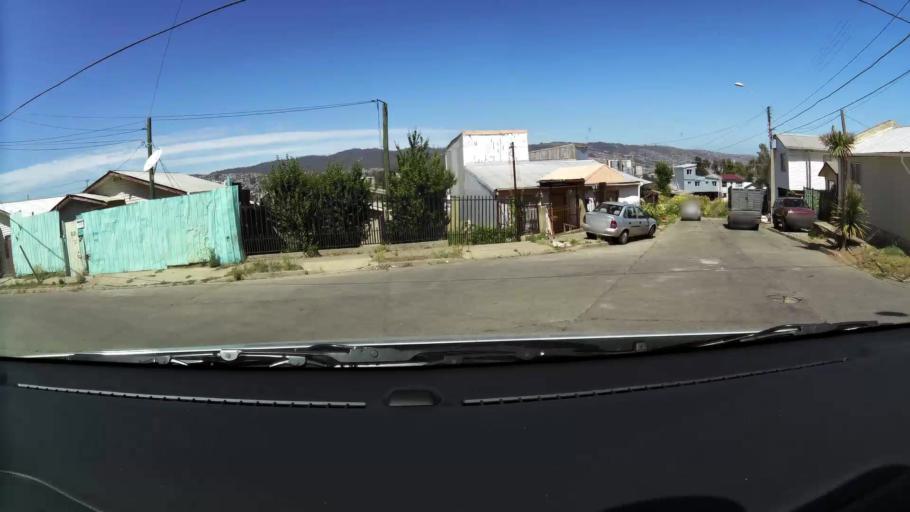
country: CL
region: Valparaiso
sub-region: Provincia de Valparaiso
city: Vina del Mar
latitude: -33.0519
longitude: -71.5825
